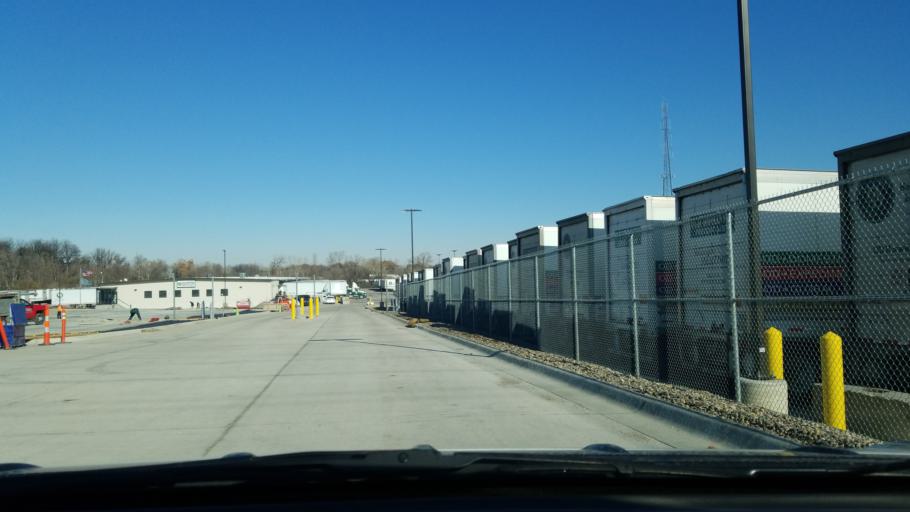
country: US
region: Nebraska
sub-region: Douglas County
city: Ralston
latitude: 41.2164
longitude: -96.0788
